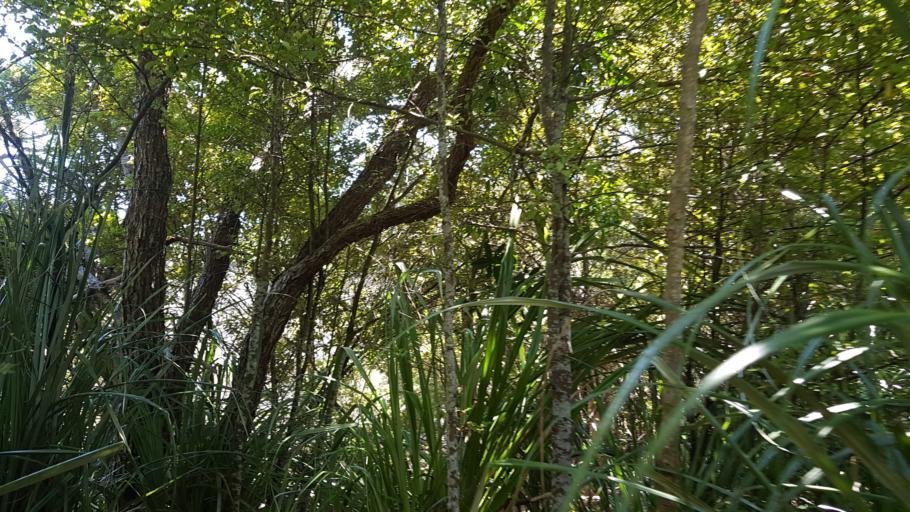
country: NZ
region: Auckland
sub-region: Auckland
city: North Shore
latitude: -36.8256
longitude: 174.7103
